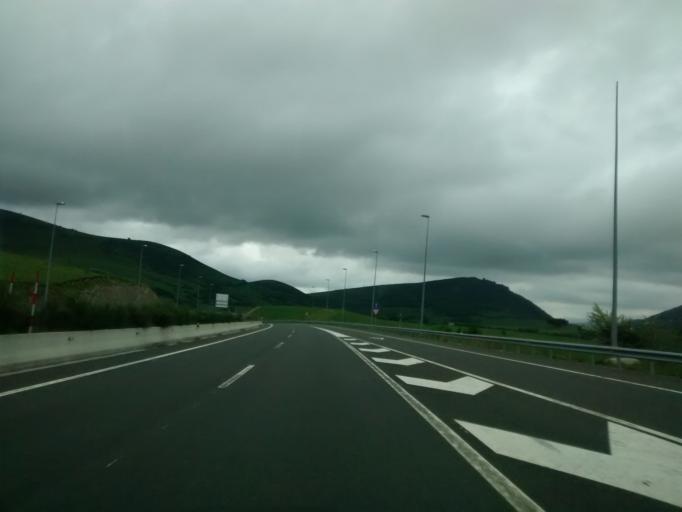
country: ES
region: Cantabria
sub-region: Provincia de Cantabria
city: Santiurde de Reinosa
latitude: 43.0706
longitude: -4.0859
